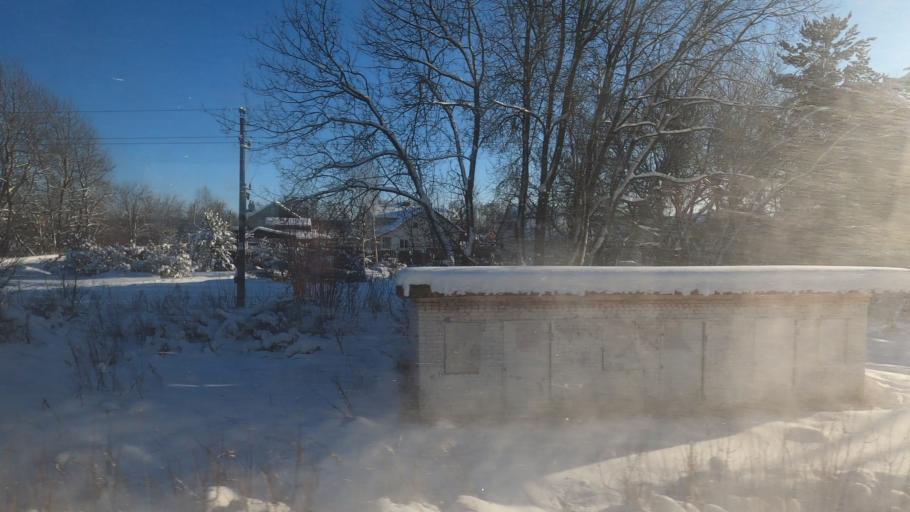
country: RU
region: Moskovskaya
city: Orud'yevo
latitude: 56.4472
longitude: 37.5210
